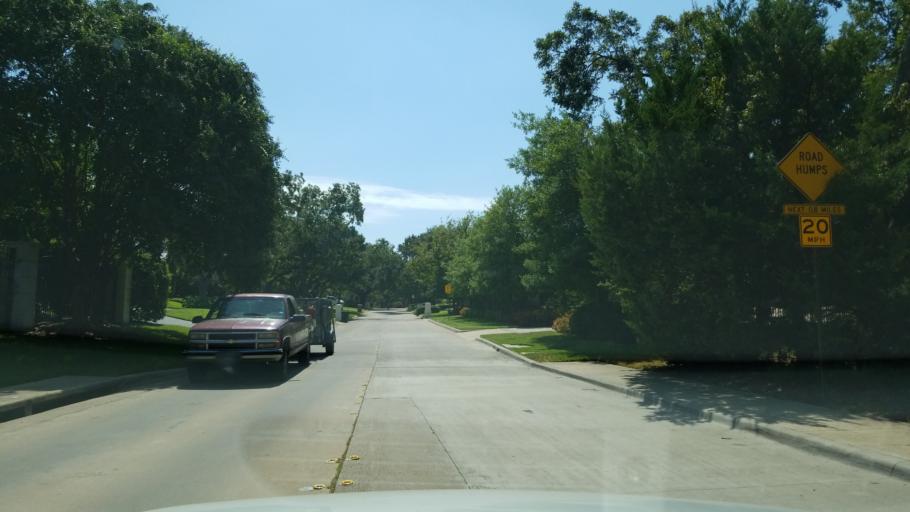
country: US
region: Texas
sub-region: Dallas County
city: Addison
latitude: 32.9531
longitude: -96.8103
